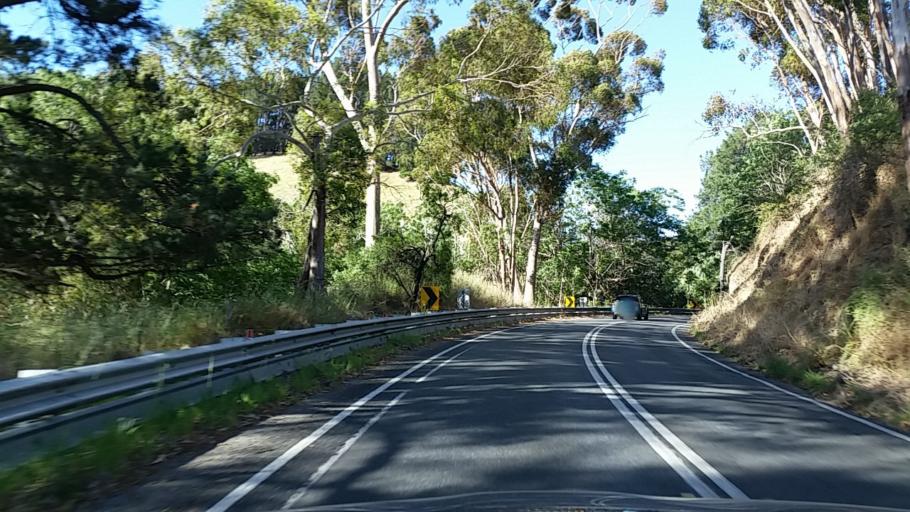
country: AU
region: South Australia
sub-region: Mount Barker
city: Meadows
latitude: -35.2365
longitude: 138.7657
